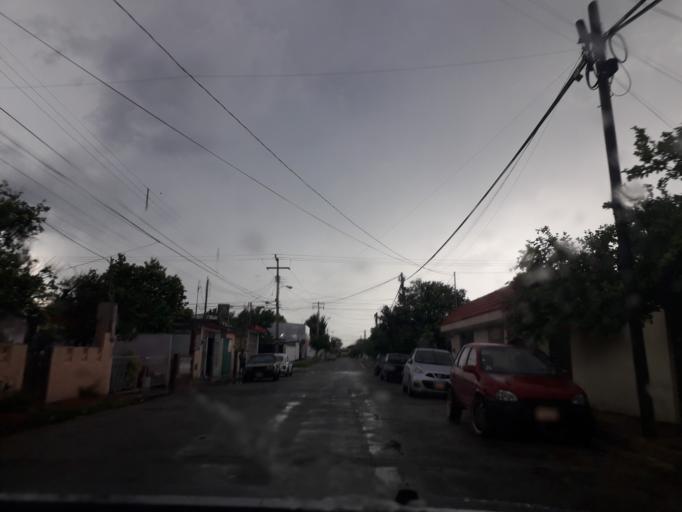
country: MX
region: Yucatan
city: Merida
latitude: 20.9808
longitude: -89.6509
